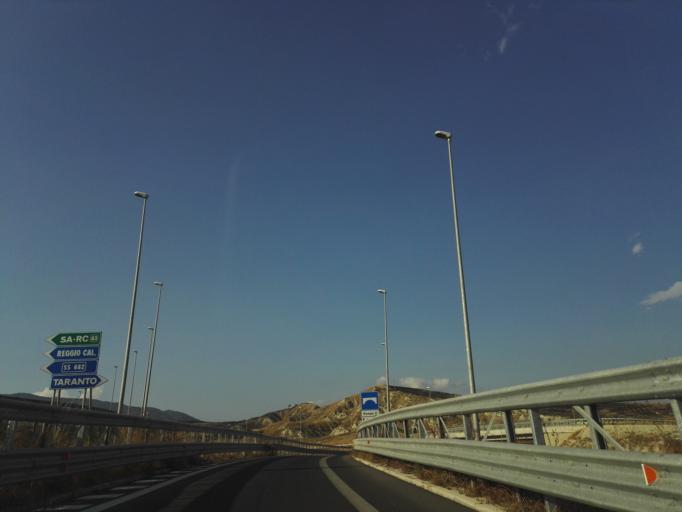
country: IT
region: Calabria
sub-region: Provincia di Reggio Calabria
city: Marina di Gioiosa Ionica
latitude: 38.3094
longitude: 16.3538
